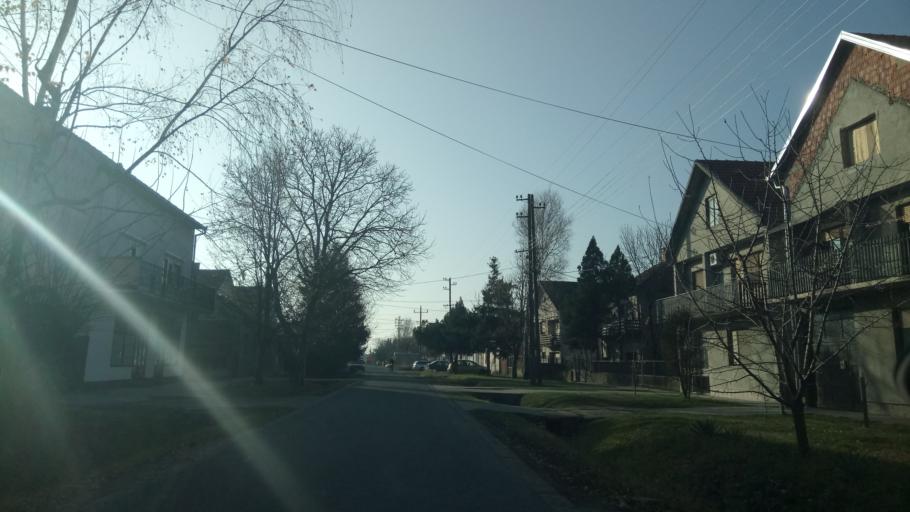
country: RS
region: Autonomna Pokrajina Vojvodina
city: Nova Pazova
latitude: 44.9397
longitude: 20.2135
